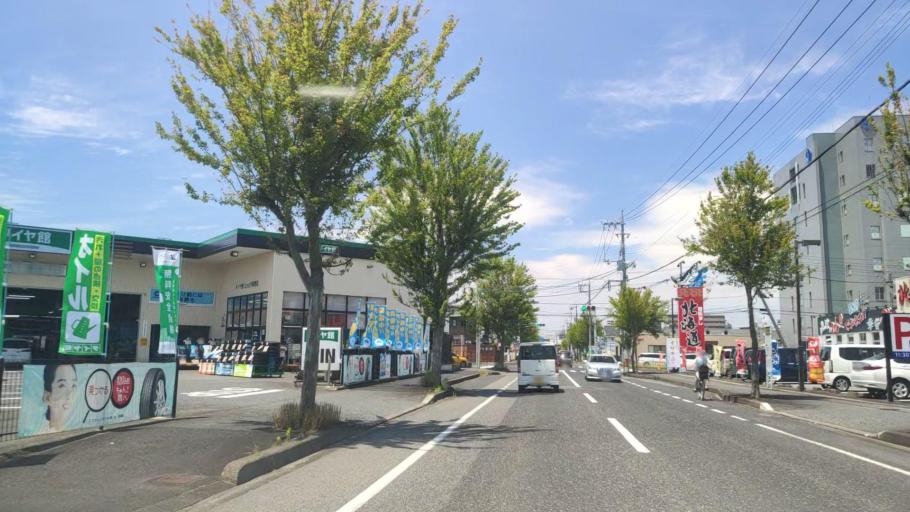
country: JP
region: Tottori
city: Tottori
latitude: 35.4857
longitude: 134.2334
